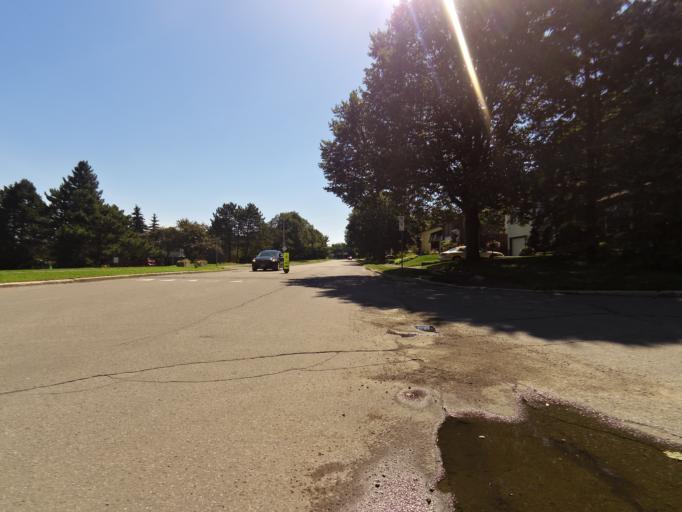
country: CA
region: Ontario
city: Ottawa
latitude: 45.3535
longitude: -75.6651
